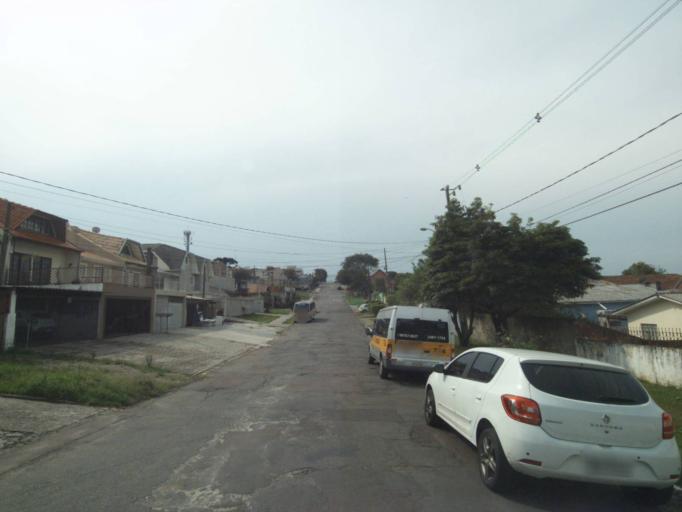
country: BR
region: Parana
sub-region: Pinhais
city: Pinhais
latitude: -25.4141
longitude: -49.2068
